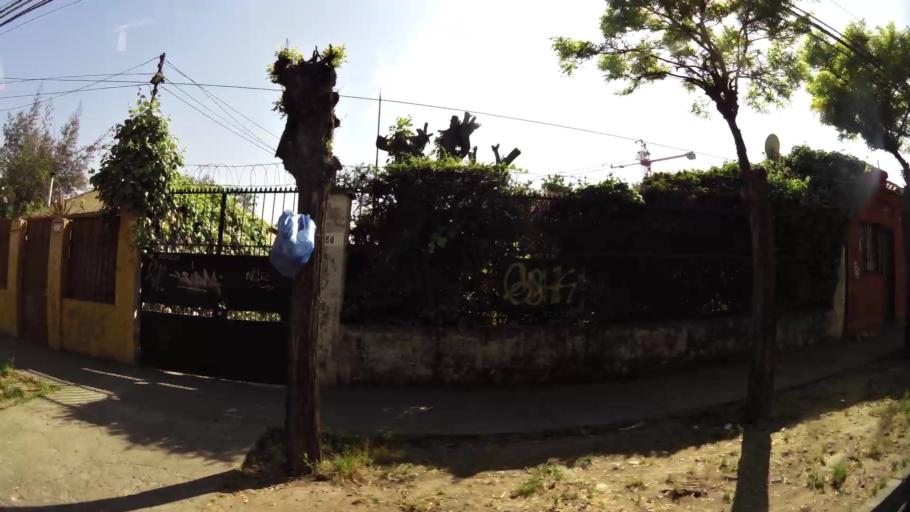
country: CL
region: Santiago Metropolitan
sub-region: Provincia de Maipo
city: San Bernardo
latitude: -33.5994
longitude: -70.7043
